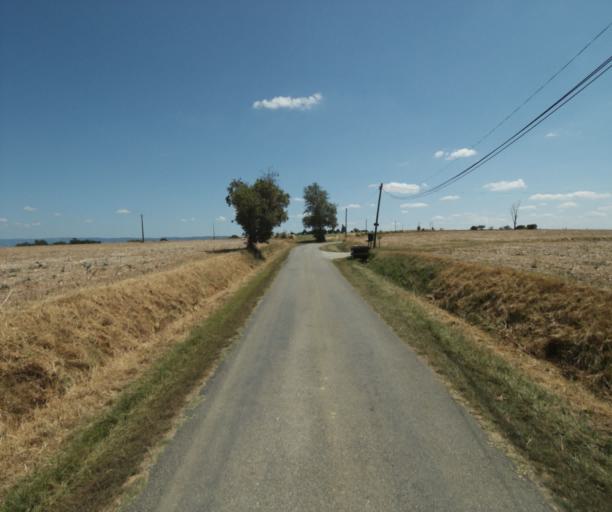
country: FR
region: Midi-Pyrenees
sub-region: Departement de la Haute-Garonne
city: Saint-Felix-Lauragais
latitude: 43.4864
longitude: 1.8608
